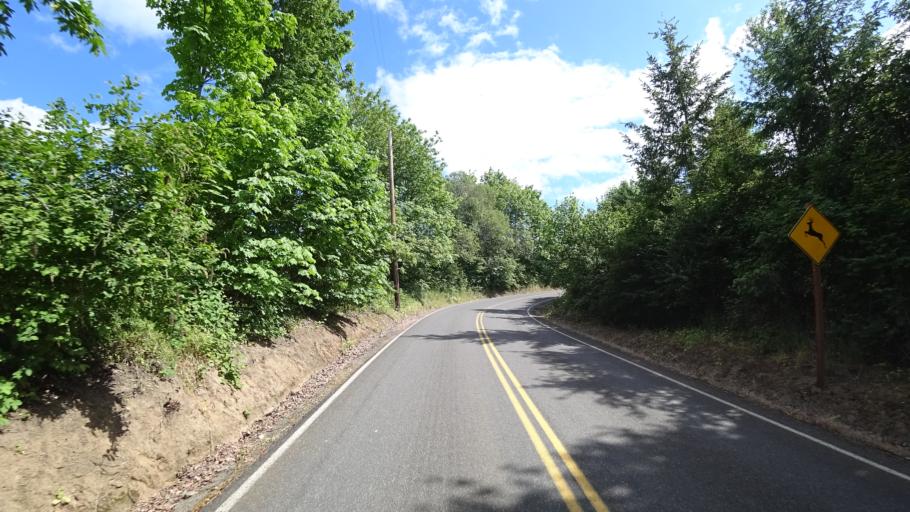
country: US
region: Oregon
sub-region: Washington County
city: Bethany
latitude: 45.6124
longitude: -122.8176
